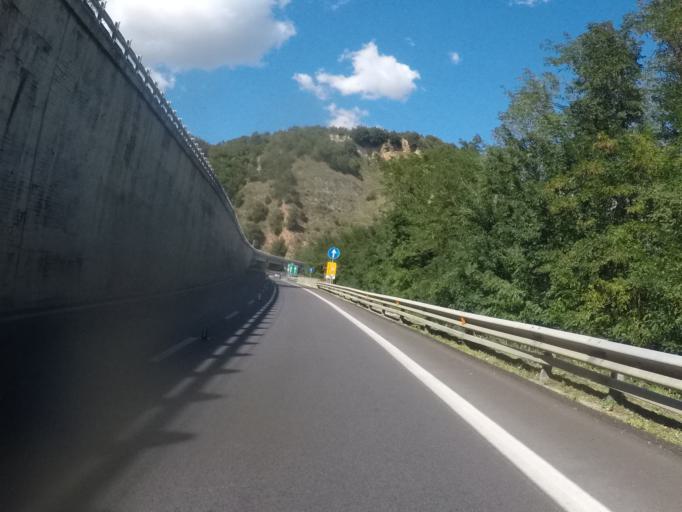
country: IT
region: Calabria
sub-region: Provincia di Cosenza
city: Altilia
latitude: 39.1401
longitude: 16.2747
